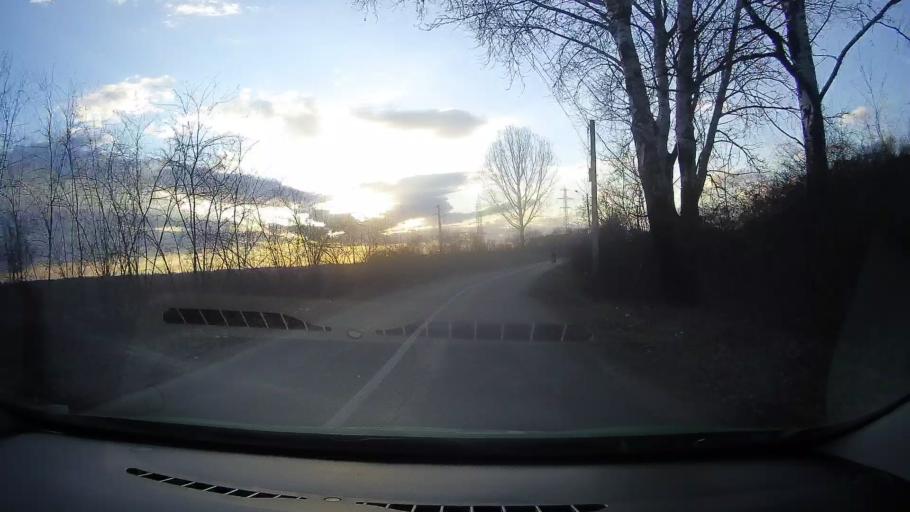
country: RO
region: Dambovita
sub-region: Comuna Gura Ocnitei
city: Gura Ocnitei
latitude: 44.9360
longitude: 25.5895
